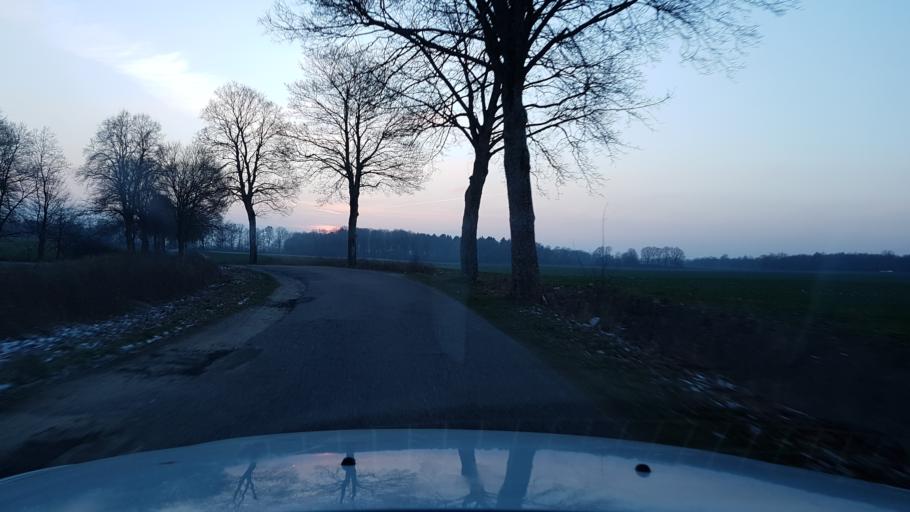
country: PL
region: West Pomeranian Voivodeship
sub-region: Powiat bialogardzki
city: Karlino
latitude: 54.0208
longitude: 15.8533
